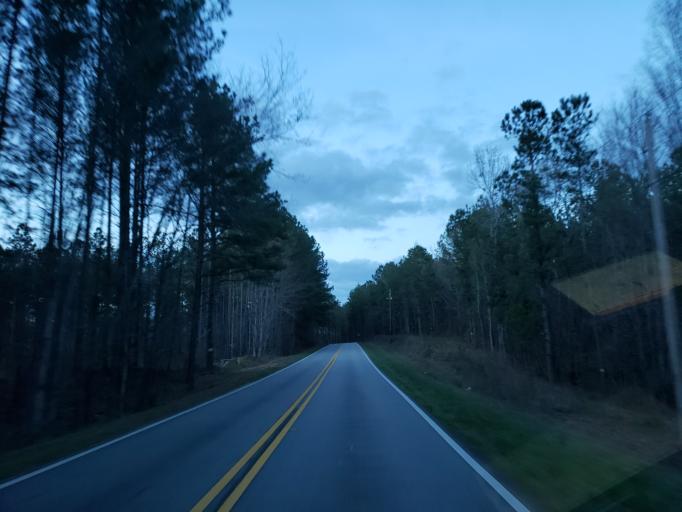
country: US
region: Georgia
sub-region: Paulding County
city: Dallas
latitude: 33.9930
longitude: -84.9247
